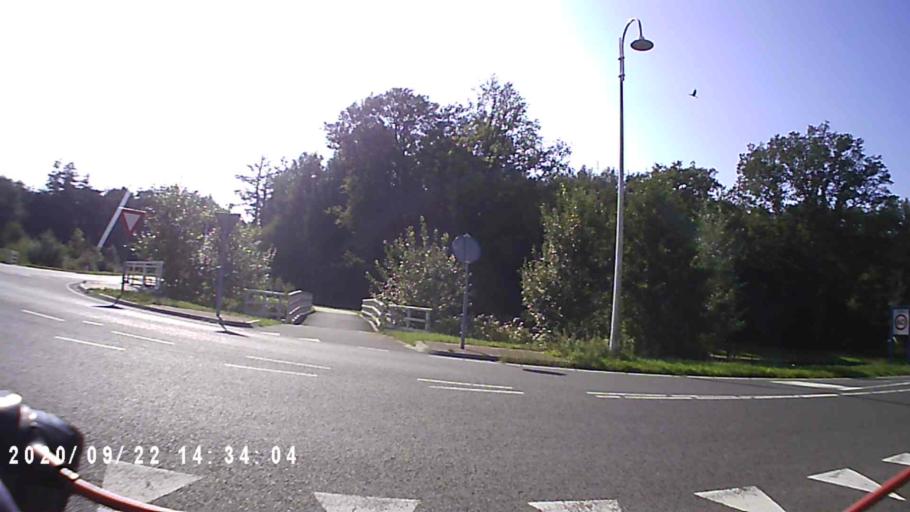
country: NL
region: Groningen
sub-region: Gemeente Leek
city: Leek
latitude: 53.0375
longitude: 6.3728
